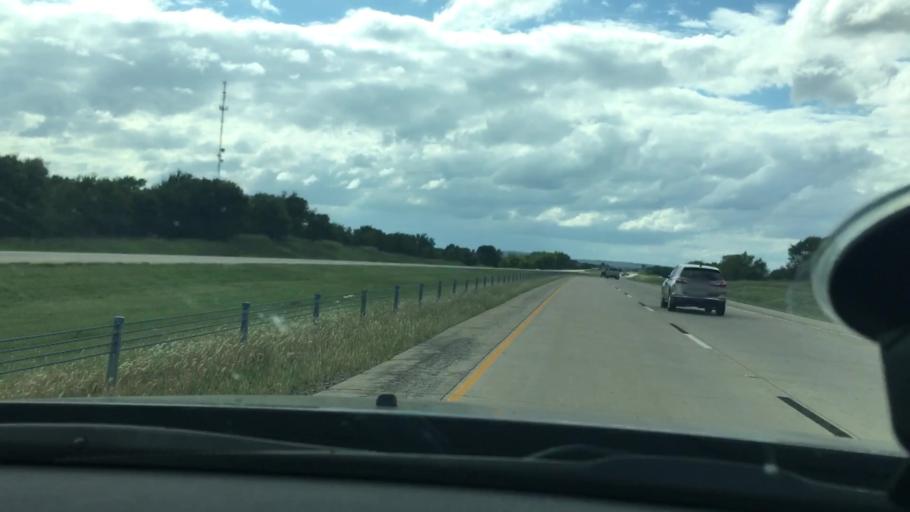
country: US
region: Oklahoma
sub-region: McIntosh County
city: Checotah
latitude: 35.4545
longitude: -95.6520
